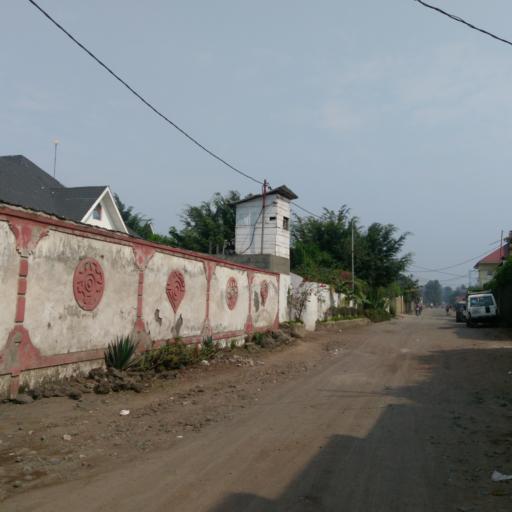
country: CD
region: Nord Kivu
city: Goma
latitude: -1.6896
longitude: 29.2343
